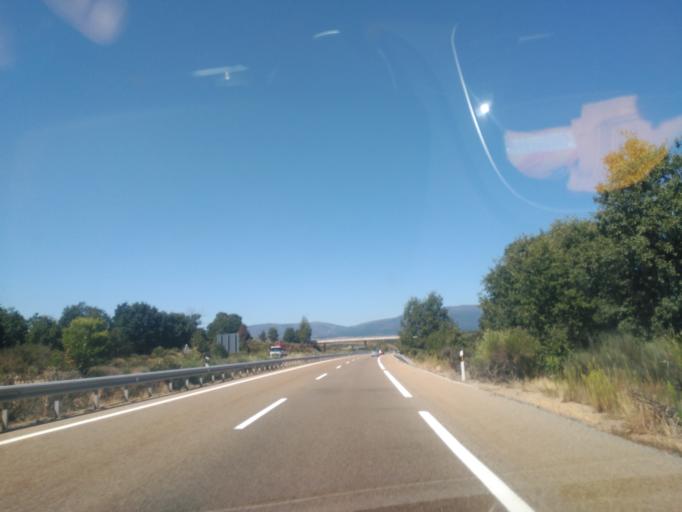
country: ES
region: Castille and Leon
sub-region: Provincia de Zamora
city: Robleda-Cervantes
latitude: 42.0552
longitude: -6.5762
